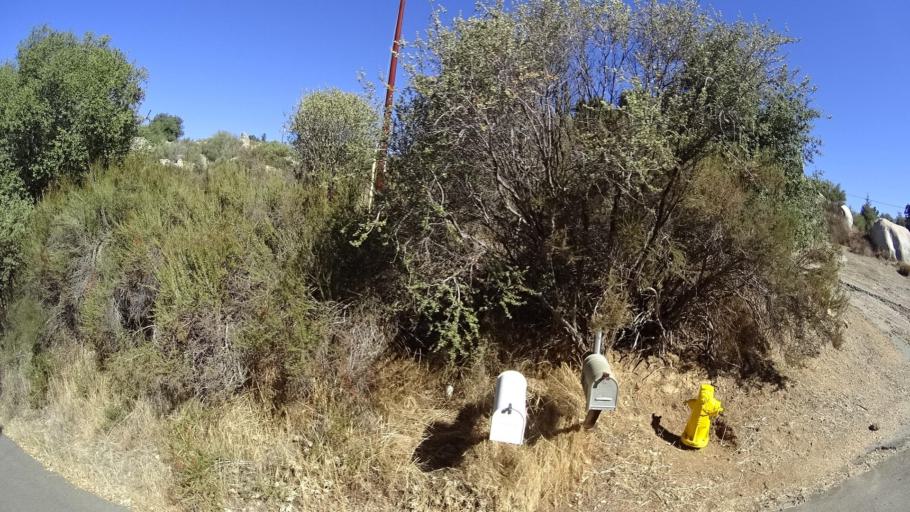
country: US
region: California
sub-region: San Diego County
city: Descanso
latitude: 32.8582
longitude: -116.6070
